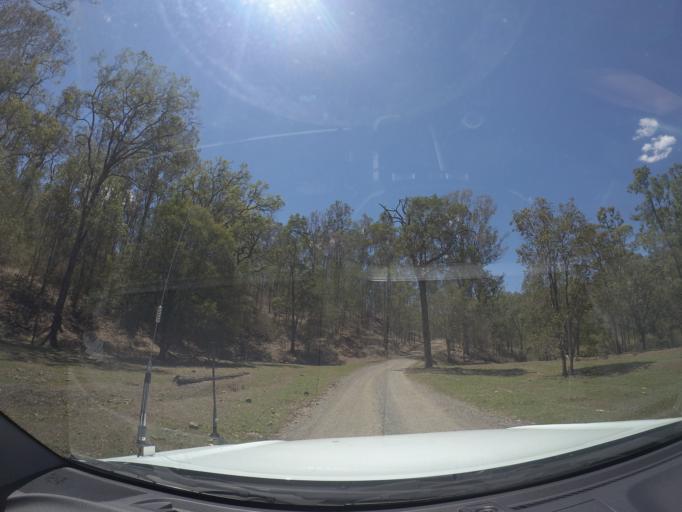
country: AU
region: Queensland
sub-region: Ipswich
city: Deebing Heights
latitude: -27.7619
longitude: 152.8077
